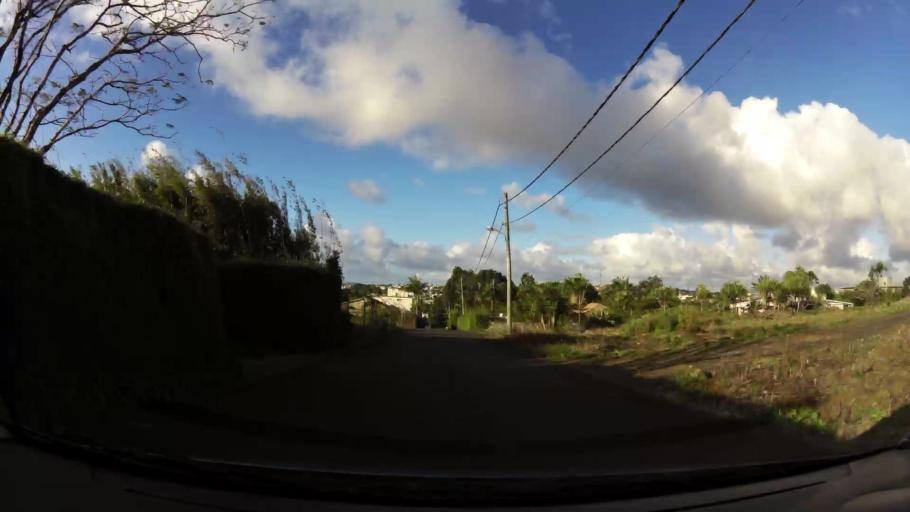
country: MU
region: Plaines Wilhems
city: Curepipe
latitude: -20.3151
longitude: 57.5153
